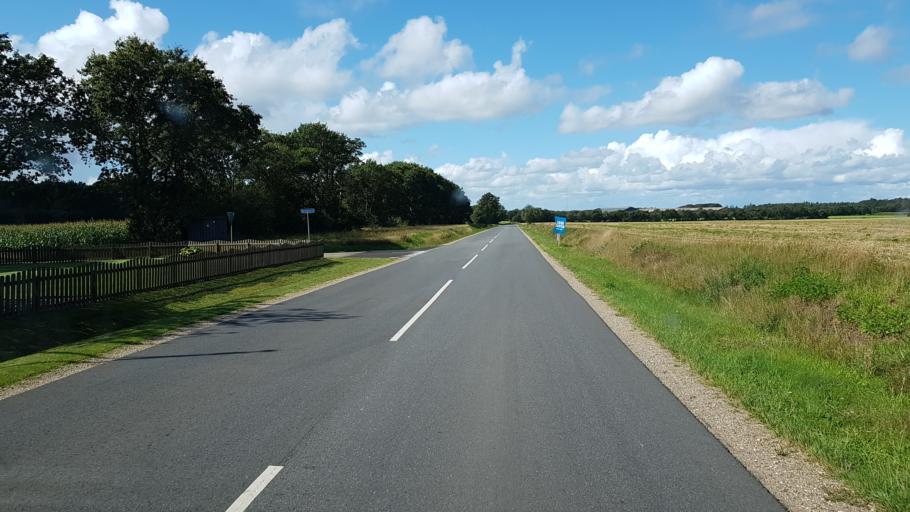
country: DK
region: South Denmark
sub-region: Esbjerg Kommune
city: Bramming
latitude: 55.6113
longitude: 8.7707
